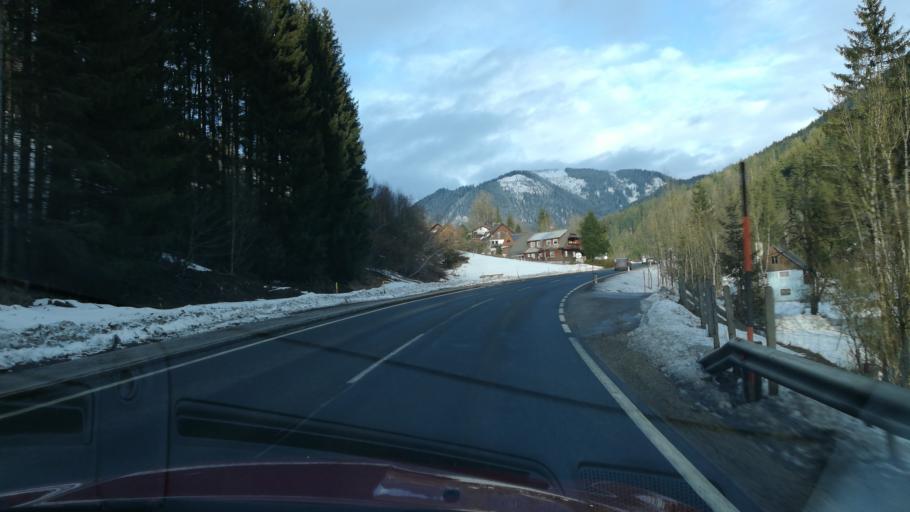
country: AT
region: Styria
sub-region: Politischer Bezirk Liezen
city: Liezen
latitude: 47.5785
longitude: 14.2610
